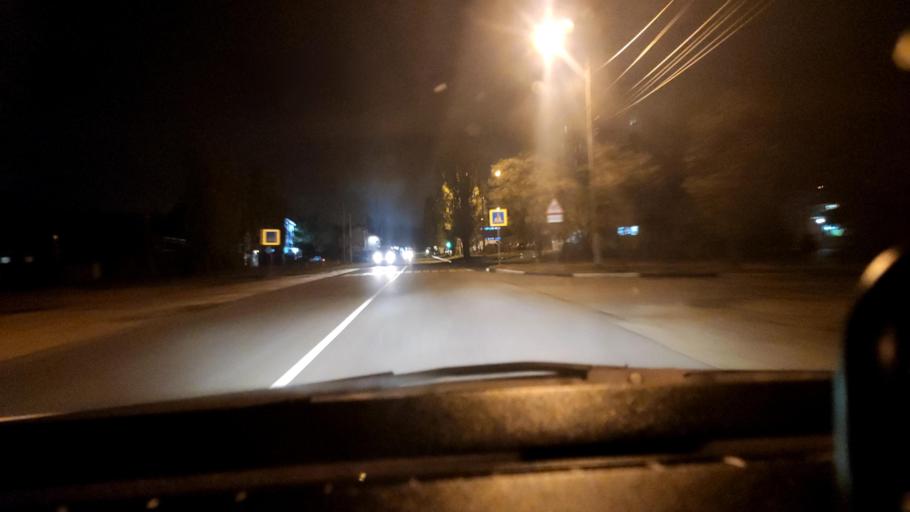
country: RU
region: Voronezj
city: Shilovo
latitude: 51.5502
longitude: 39.0878
